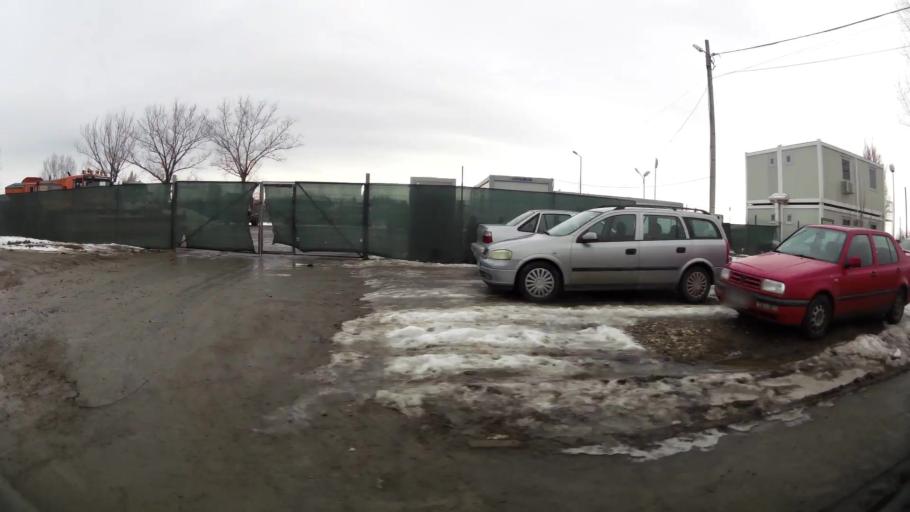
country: RO
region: Ilfov
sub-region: Comuna Pantelimon
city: Pantelimon
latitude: 44.4529
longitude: 26.2118
